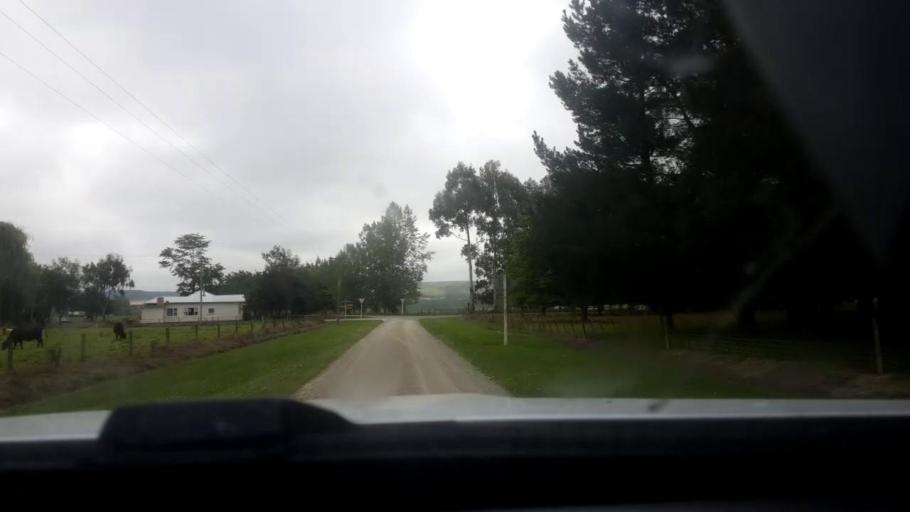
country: NZ
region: Canterbury
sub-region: Timaru District
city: Pleasant Point
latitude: -44.2078
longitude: 171.1129
